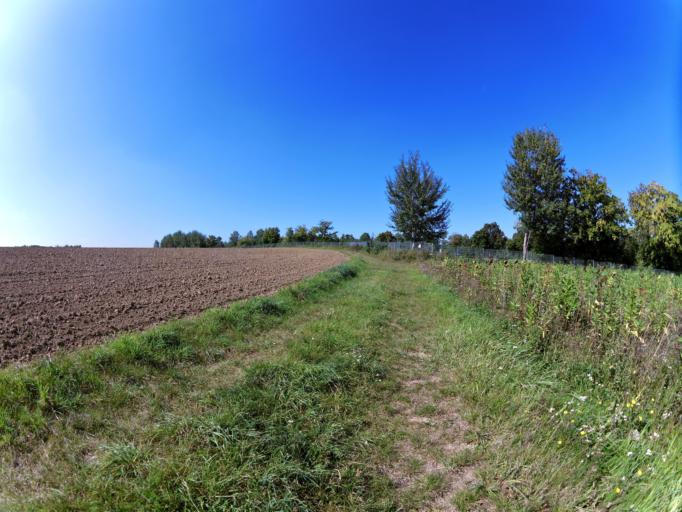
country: DE
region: Bavaria
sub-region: Regierungsbezirk Unterfranken
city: Kleinrinderfeld
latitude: 49.7039
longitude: 9.8018
